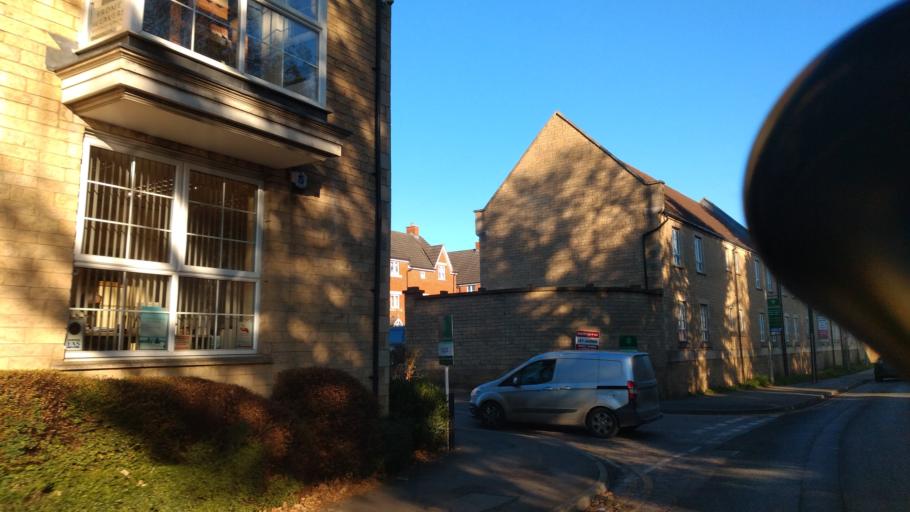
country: GB
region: England
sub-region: Somerset
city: Frome
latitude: 51.2286
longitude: -2.3089
